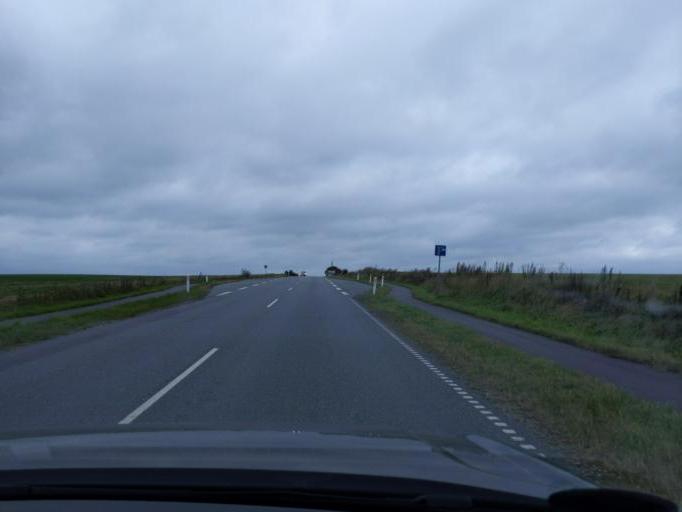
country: DK
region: North Denmark
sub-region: Mariagerfjord Kommune
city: Hobro
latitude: 56.5929
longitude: 9.7781
